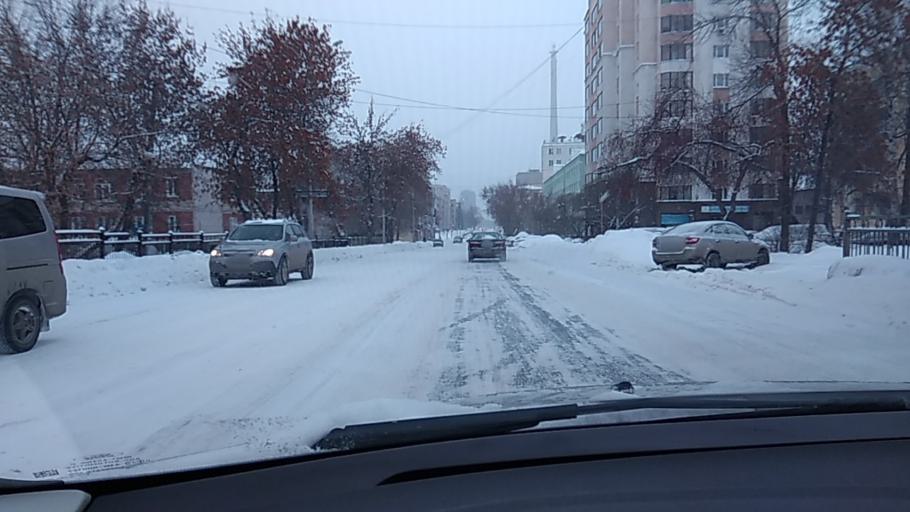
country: RU
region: Sverdlovsk
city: Yekaterinburg
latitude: 56.8160
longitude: 60.6105
